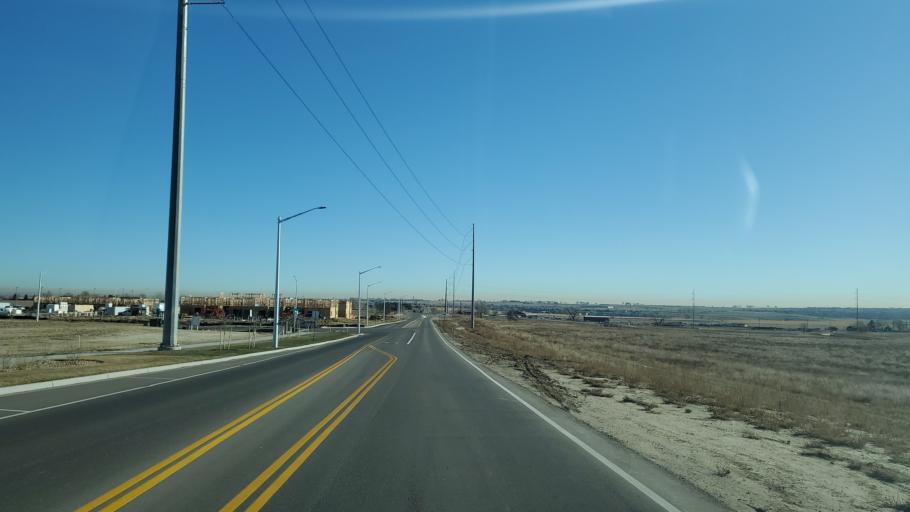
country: US
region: Colorado
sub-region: Boulder County
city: Erie
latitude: 39.9866
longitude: -104.9850
